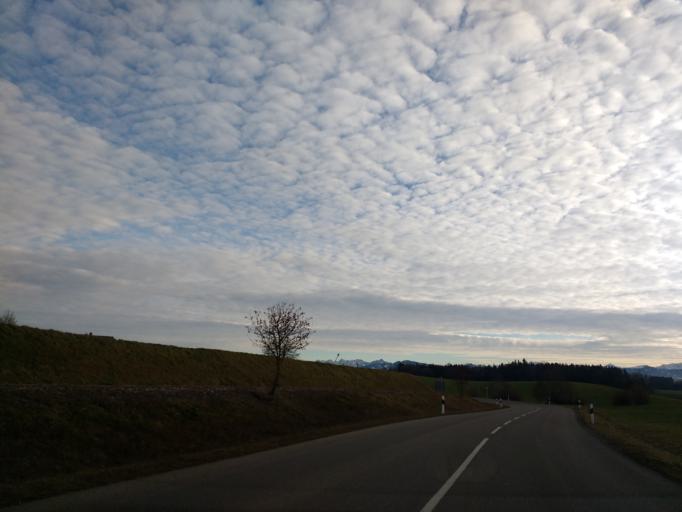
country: DE
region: Bavaria
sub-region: Swabia
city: Neuburg
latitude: 47.7782
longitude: 10.3576
